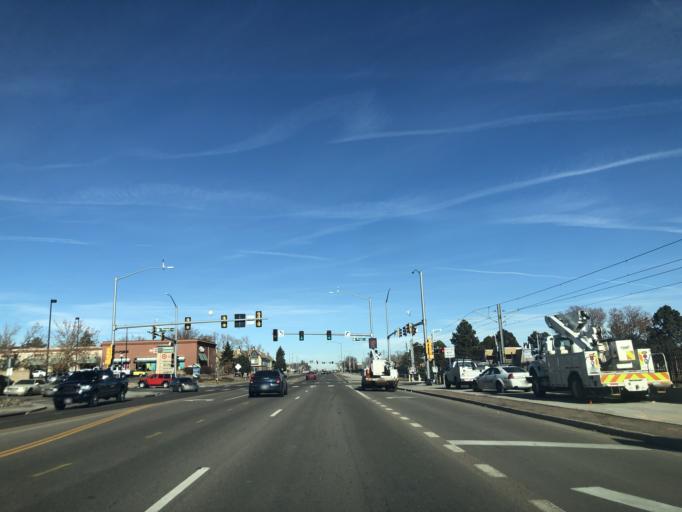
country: US
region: Colorado
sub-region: Adams County
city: Aurora
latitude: 39.7134
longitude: -104.8193
